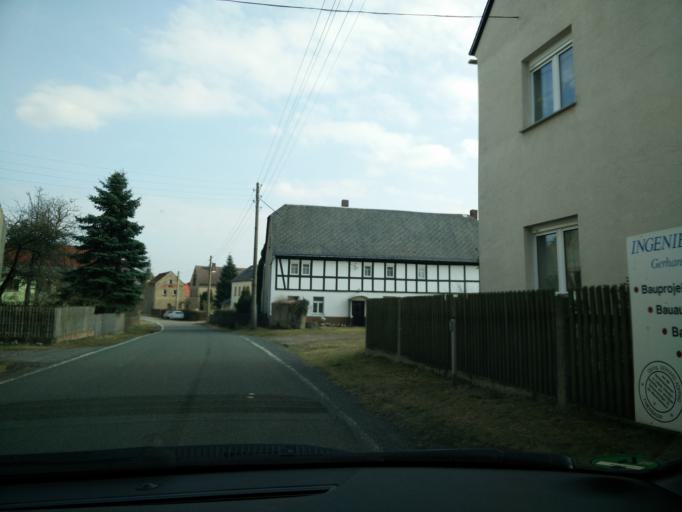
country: DE
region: Saxony
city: Konigsfeld
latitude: 51.1063
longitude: 12.7303
